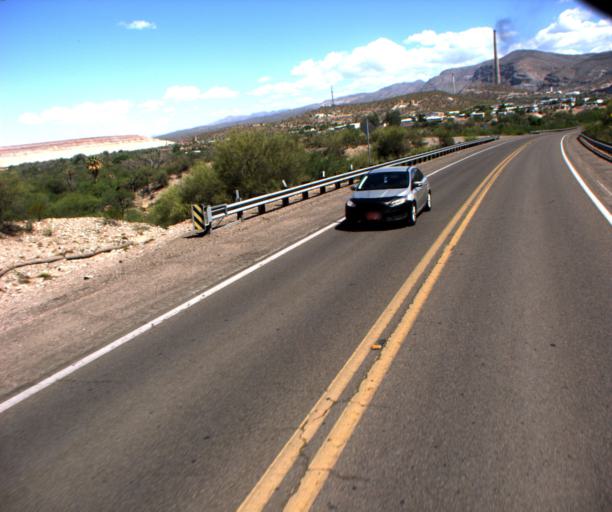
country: US
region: Arizona
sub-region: Pinal County
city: Kearny
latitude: 32.9807
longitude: -110.7694
